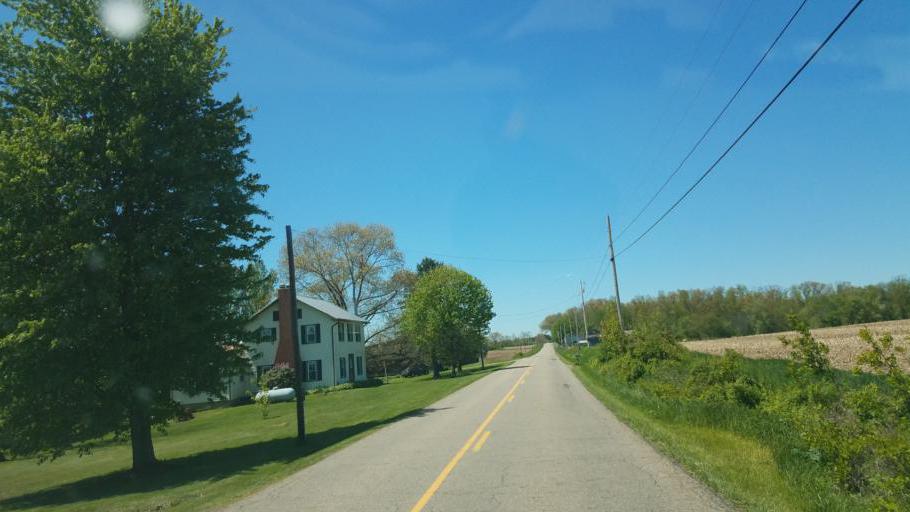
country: US
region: Ohio
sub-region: Knox County
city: Fredericktown
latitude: 40.4951
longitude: -82.4908
